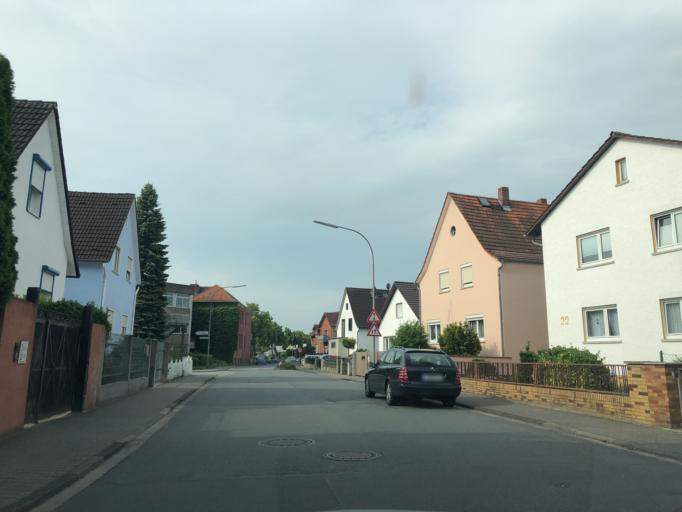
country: DE
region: Hesse
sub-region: Regierungsbezirk Darmstadt
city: Nauheim
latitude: 49.9656
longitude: 8.4523
